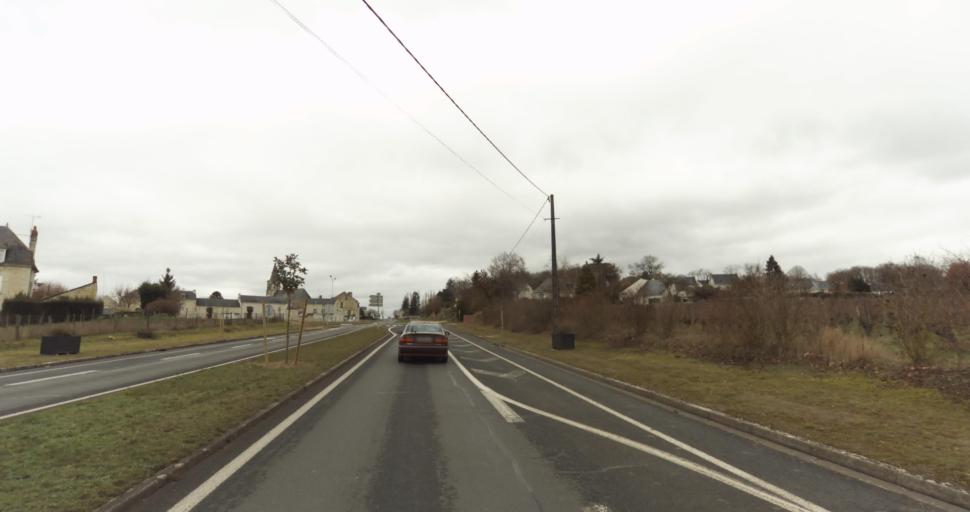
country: FR
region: Pays de la Loire
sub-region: Departement de Maine-et-Loire
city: Varrains
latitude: 47.2248
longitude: -0.0644
